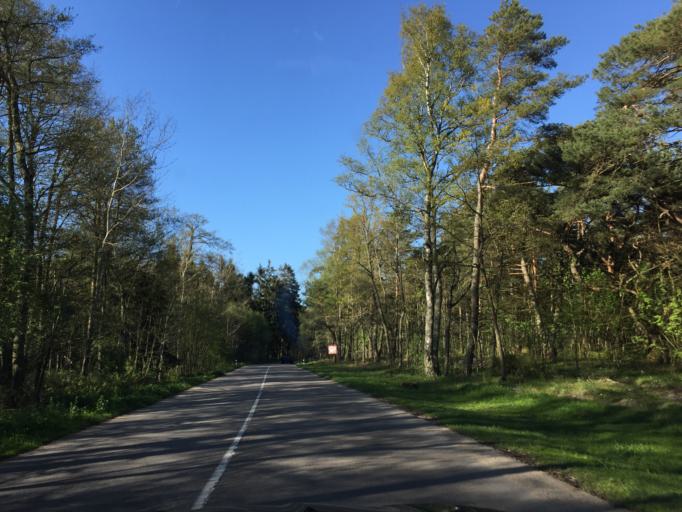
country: LT
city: Nida
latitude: 55.1891
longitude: 20.8582
